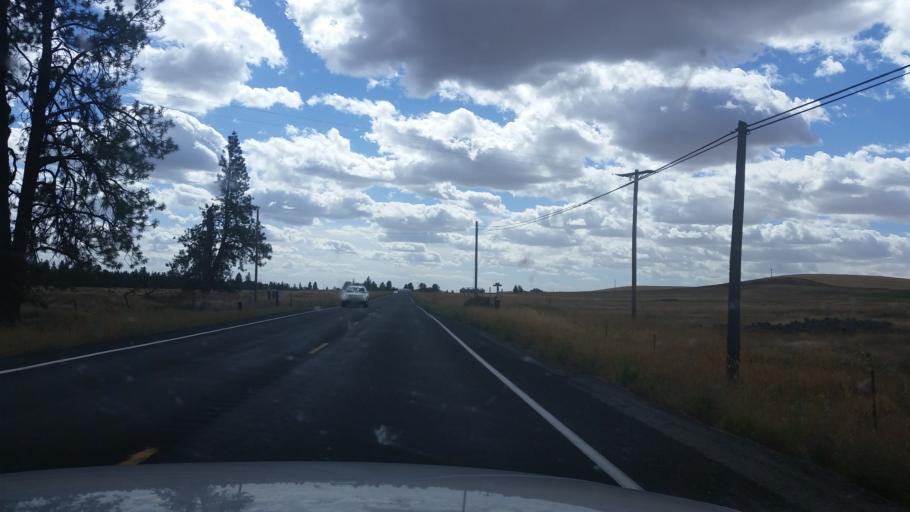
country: US
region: Washington
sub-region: Spokane County
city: Medical Lake
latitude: 47.5372
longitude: -117.7101
